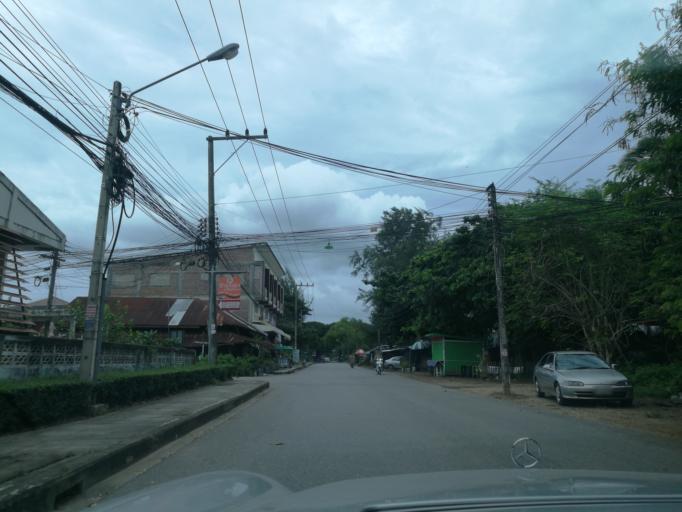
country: TH
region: Prachuap Khiri Khan
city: Prachuap Khiri Khan
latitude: 11.8109
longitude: 99.7930
